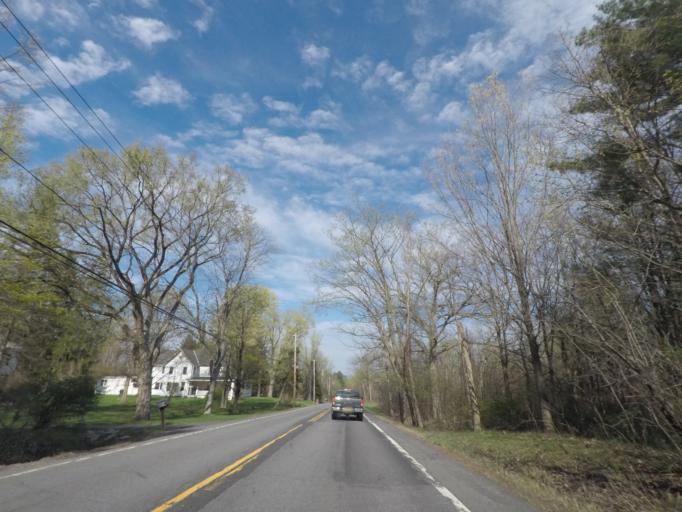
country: US
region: New York
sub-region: Albany County
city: Voorheesville
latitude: 42.6276
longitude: -73.9257
